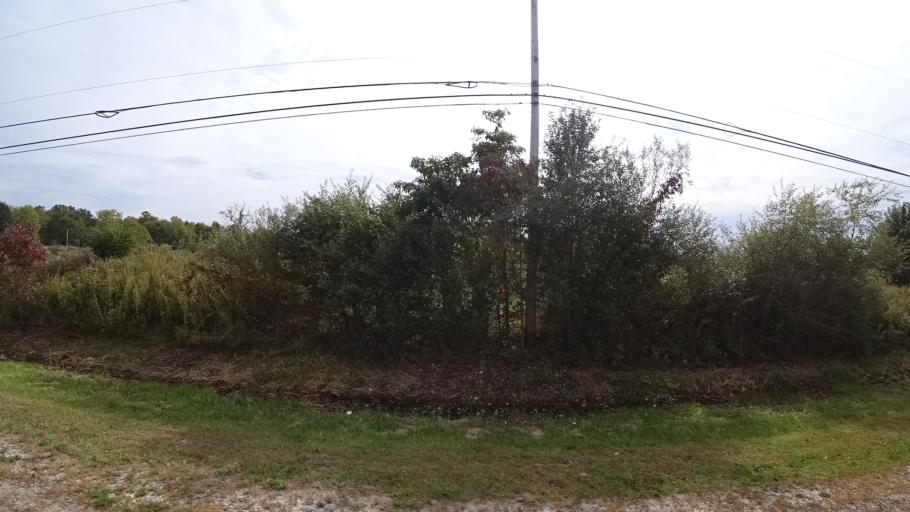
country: US
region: Indiana
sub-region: LaPorte County
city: Long Beach
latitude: 41.7235
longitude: -86.8179
